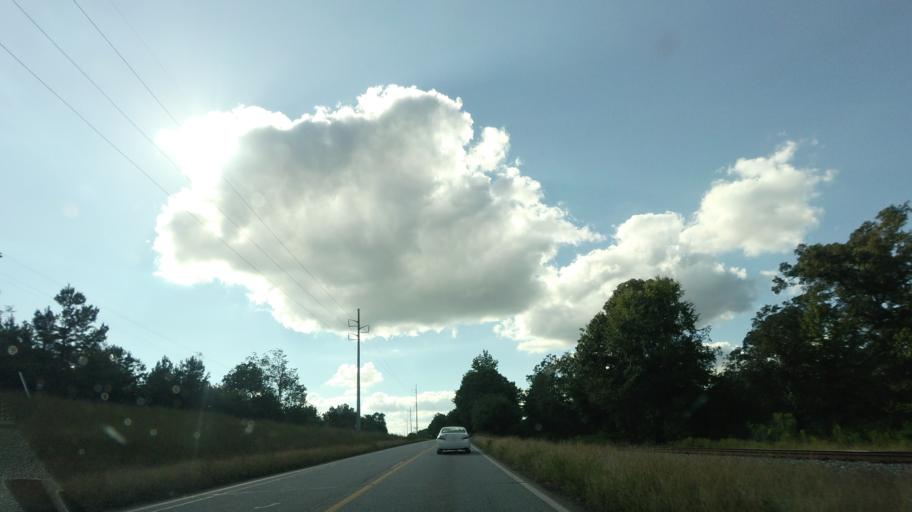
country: US
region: Georgia
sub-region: Lamar County
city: Barnesville
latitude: 33.0541
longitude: -84.0474
